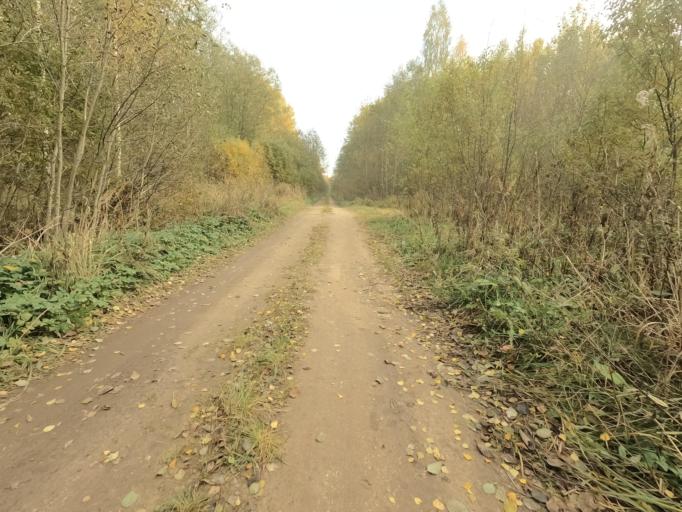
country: RU
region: Novgorod
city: Pankovka
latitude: 58.8802
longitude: 30.8412
